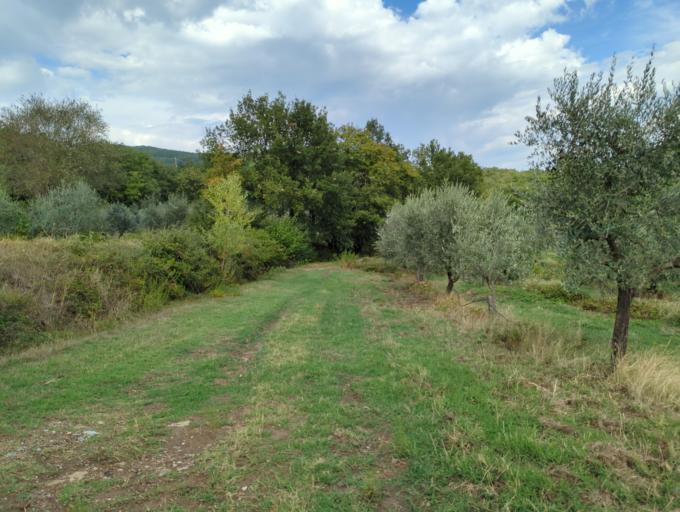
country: IT
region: Tuscany
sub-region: Province of Arezzo
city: Castiglion Fibocchi
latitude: 43.5437
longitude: 11.7659
